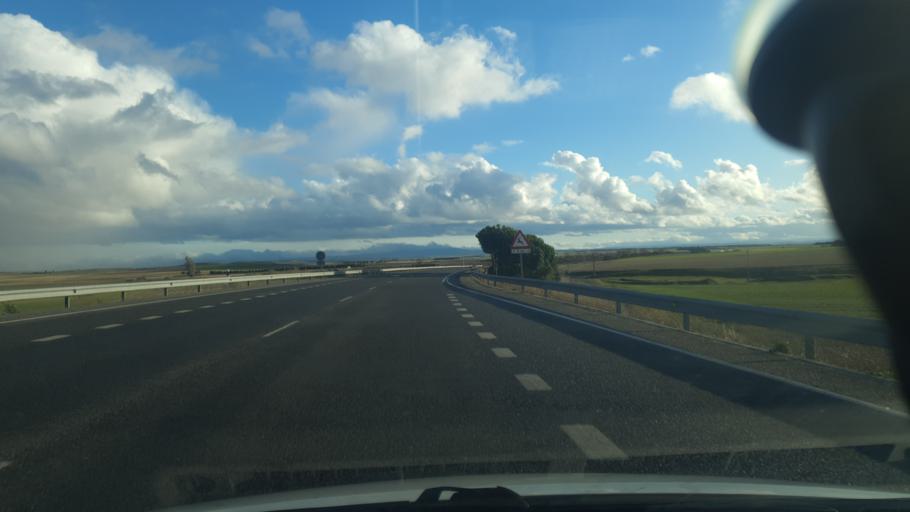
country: ES
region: Castille and Leon
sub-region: Provincia de Segovia
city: Codorniz
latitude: 41.0486
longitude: -4.6231
